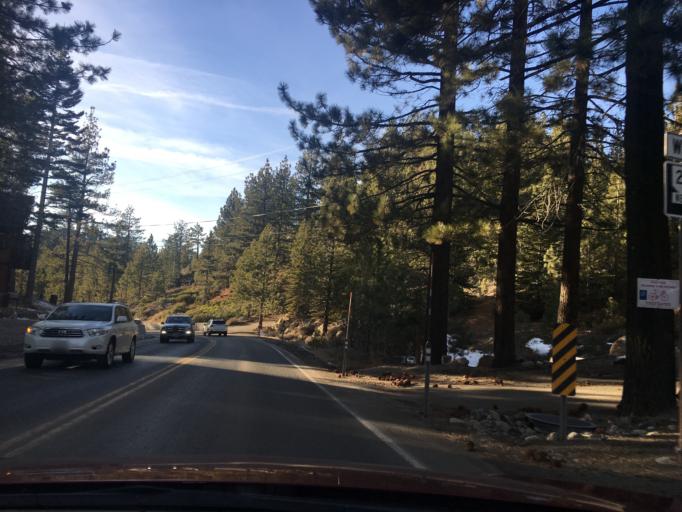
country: US
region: Nevada
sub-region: Douglas County
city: Kingsbury
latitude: 38.9767
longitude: -119.8900
